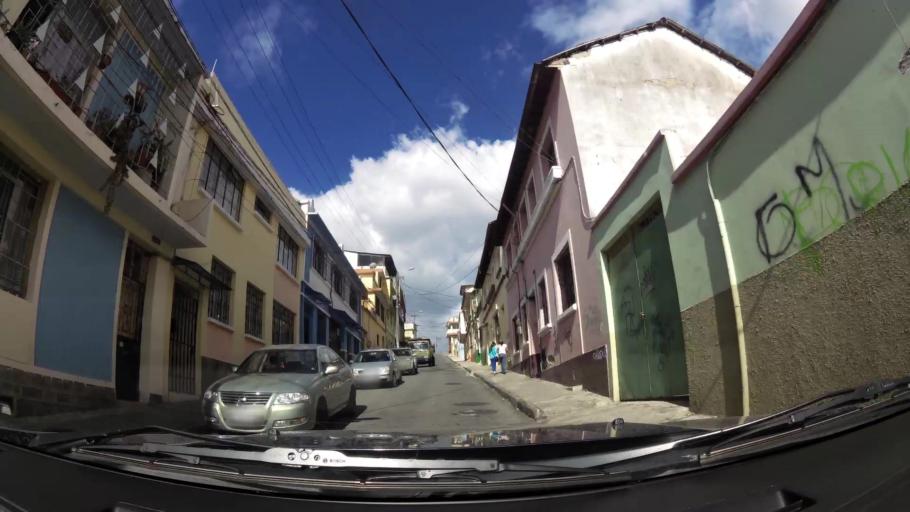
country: EC
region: Pichincha
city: Quito
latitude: -0.2266
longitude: -78.5042
